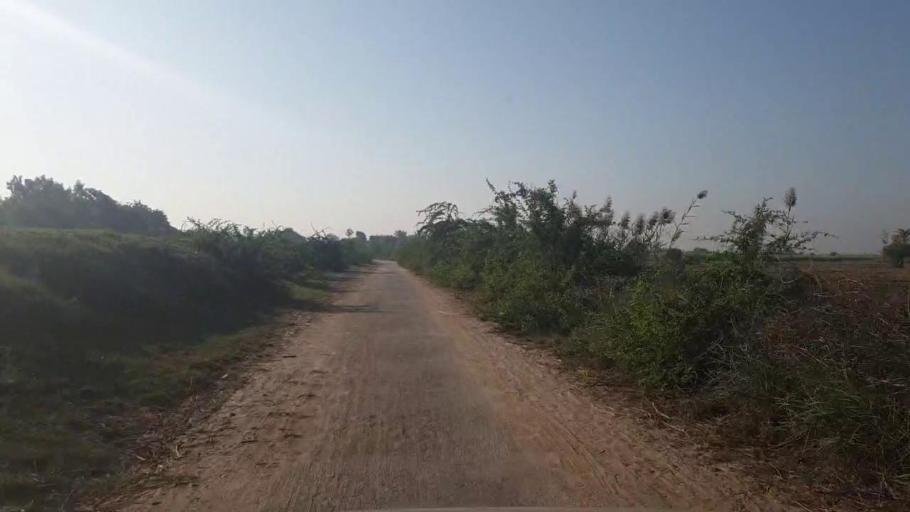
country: PK
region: Sindh
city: Tando Bago
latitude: 24.7394
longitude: 68.9303
